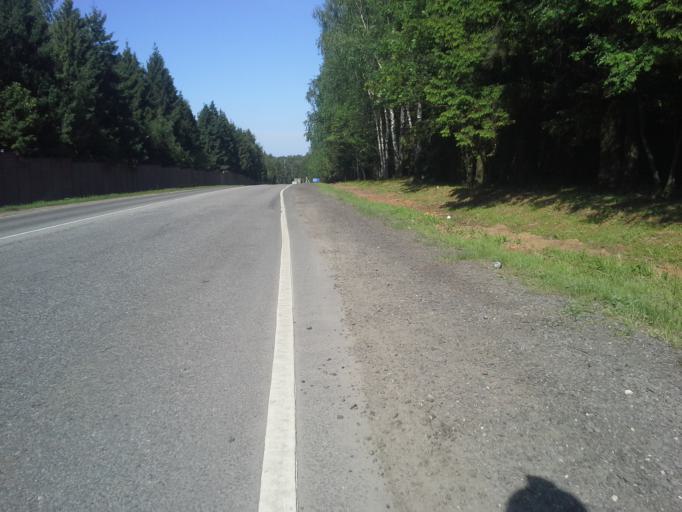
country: RU
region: Moskovskaya
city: Vatutinki
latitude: 55.4306
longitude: 37.3533
